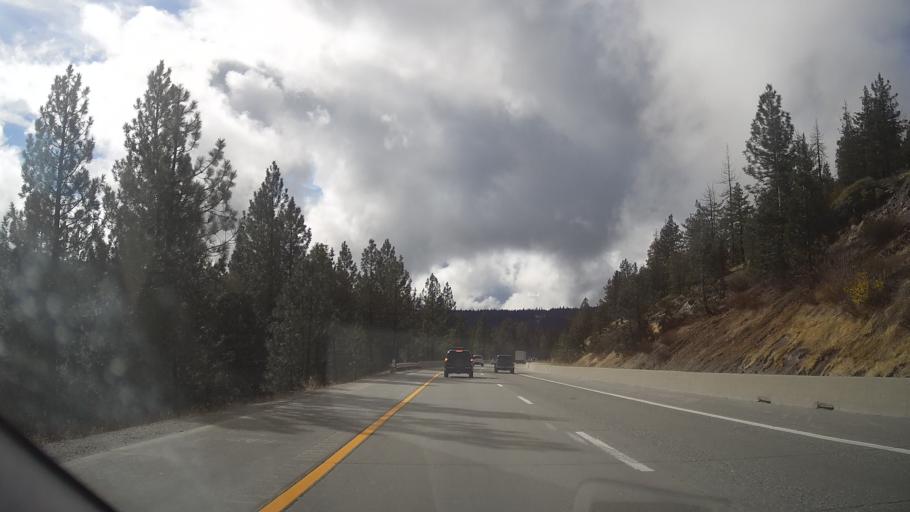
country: US
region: California
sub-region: Sierra County
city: Downieville
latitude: 39.3063
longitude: -120.6471
